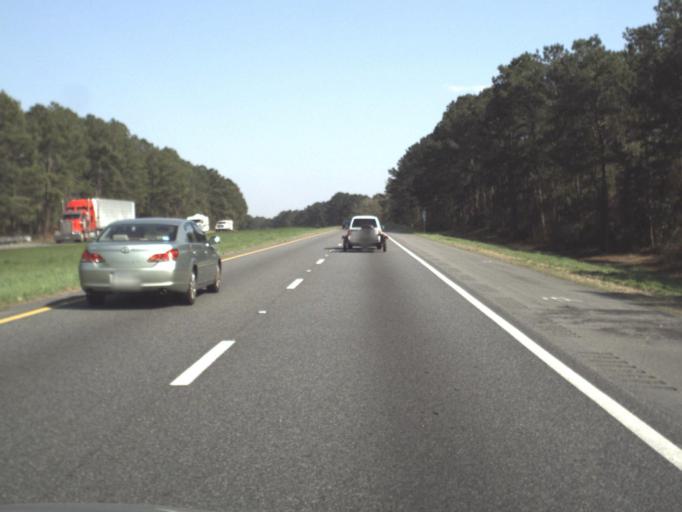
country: US
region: Florida
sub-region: Gadsden County
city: Quincy
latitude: 30.5320
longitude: -84.5741
